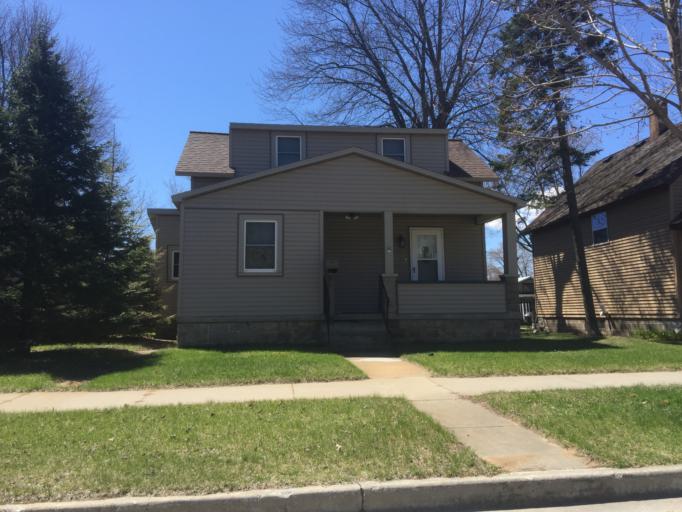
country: US
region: Michigan
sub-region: Menominee County
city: Menominee
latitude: 45.0900
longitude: -87.6099
